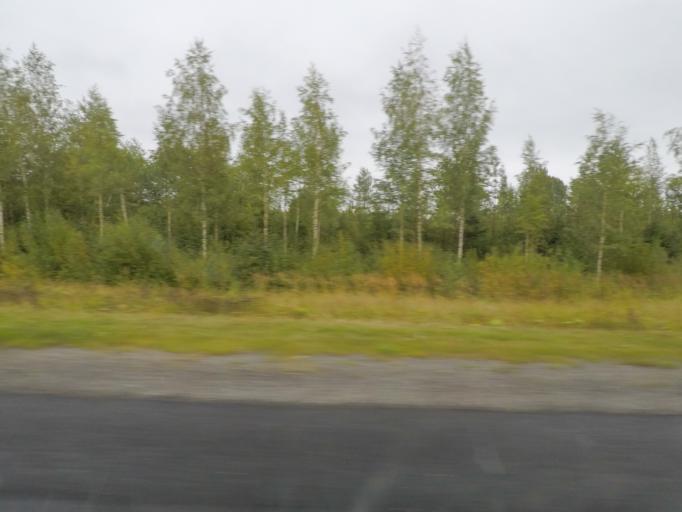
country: FI
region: Northern Savo
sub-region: Kuopio
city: Kuopio
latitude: 62.6922
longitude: 27.5695
